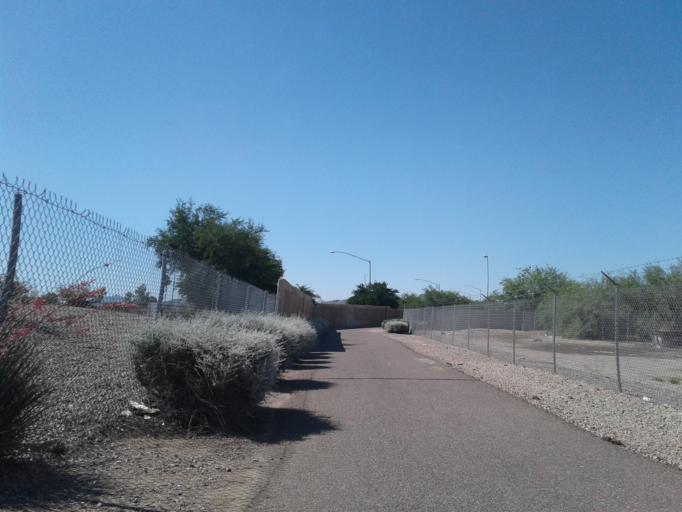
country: US
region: Arizona
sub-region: Maricopa County
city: Paradise Valley
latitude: 33.6250
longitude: -112.0083
